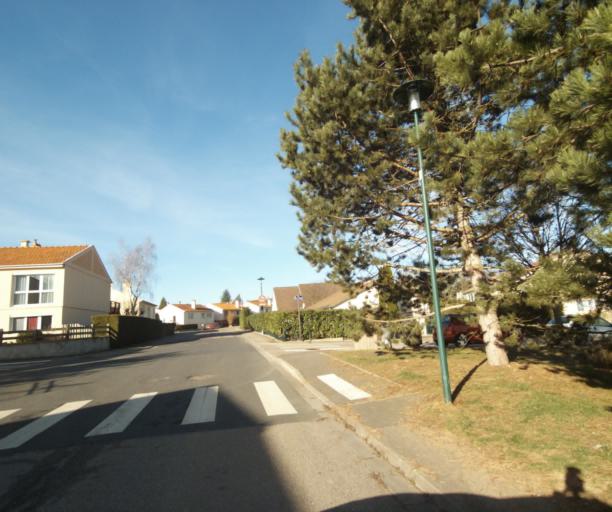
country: FR
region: Lorraine
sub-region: Departement de Meurthe-et-Moselle
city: Chavigny
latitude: 48.6559
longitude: 6.1211
